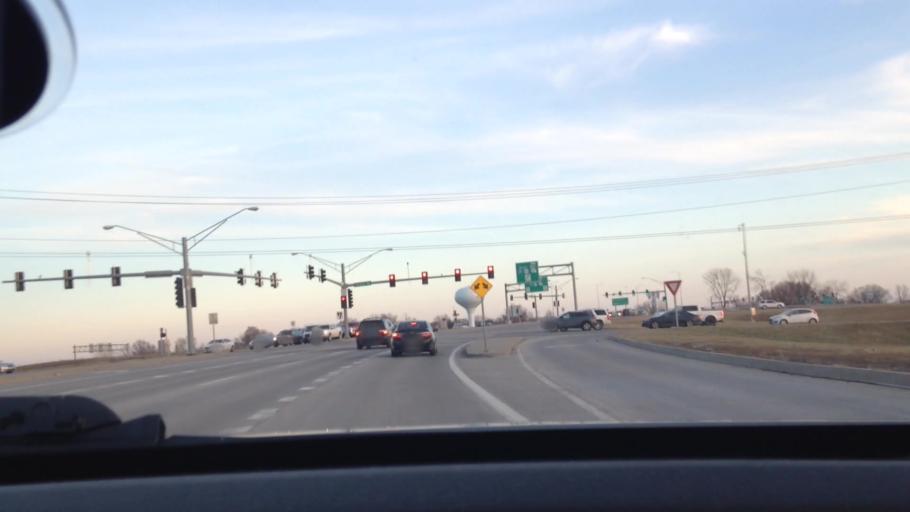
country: US
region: Missouri
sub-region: Clay County
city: Liberty
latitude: 39.2665
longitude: -94.4490
